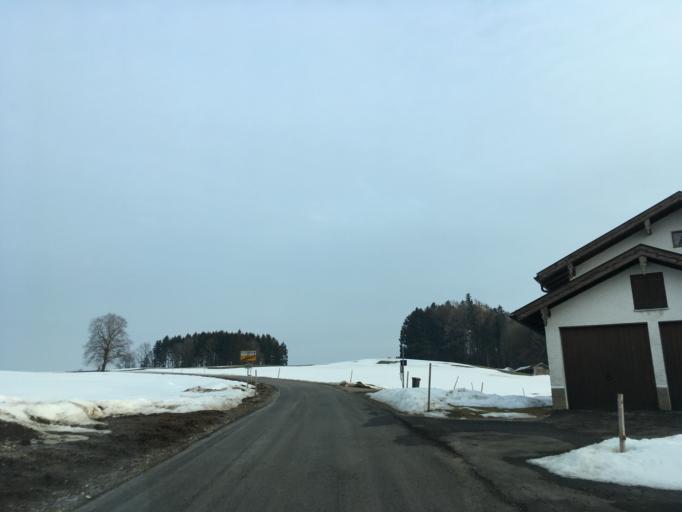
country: DE
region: Bavaria
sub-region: Upper Bavaria
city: Bad Endorf
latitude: 47.9201
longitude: 12.3168
